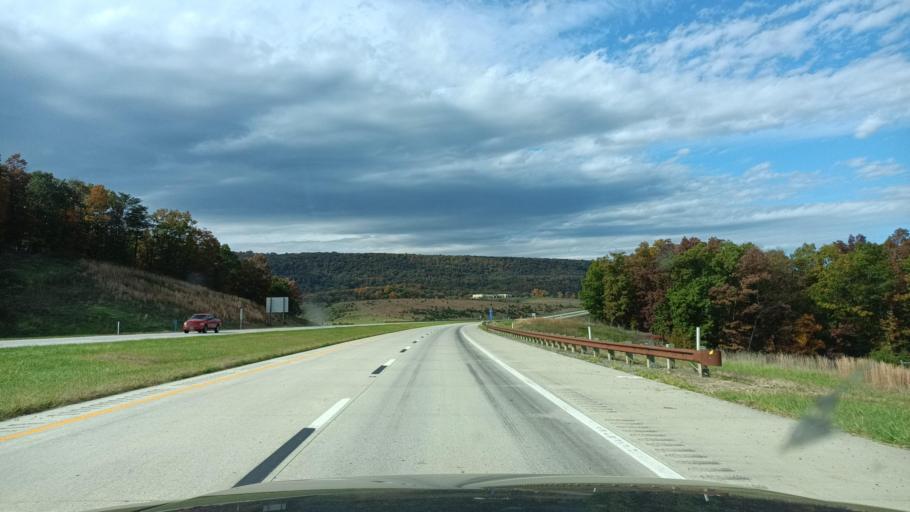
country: US
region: West Virginia
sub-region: Hardy County
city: Moorefield
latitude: 39.0889
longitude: -78.9813
